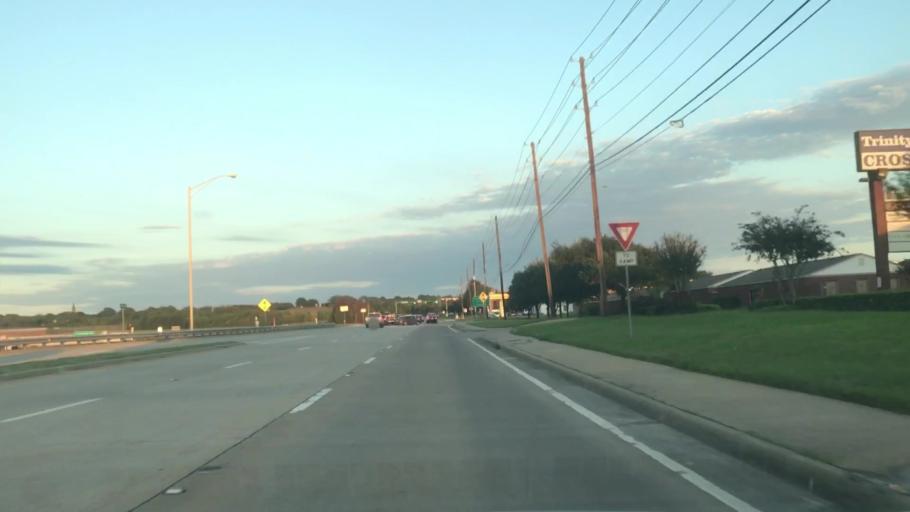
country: US
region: Texas
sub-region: Dallas County
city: Carrollton
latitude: 32.9851
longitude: -96.8719
